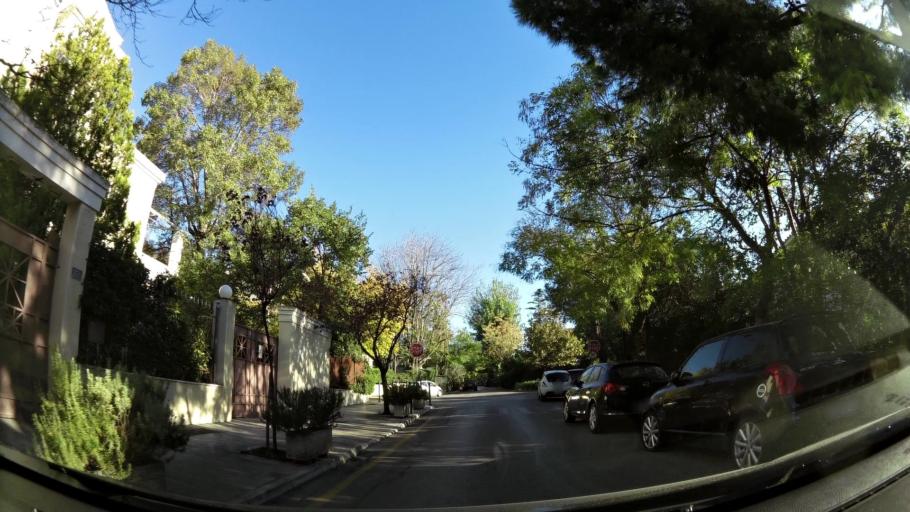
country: GR
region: Attica
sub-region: Nomarchia Athinas
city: Kifisia
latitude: 38.0754
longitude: 23.8158
